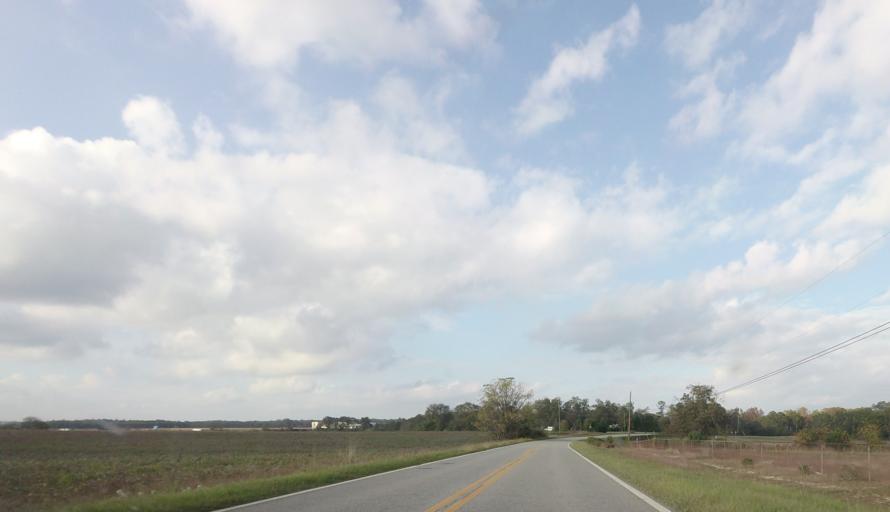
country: US
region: Georgia
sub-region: Peach County
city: Byron
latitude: 32.7197
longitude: -83.7232
